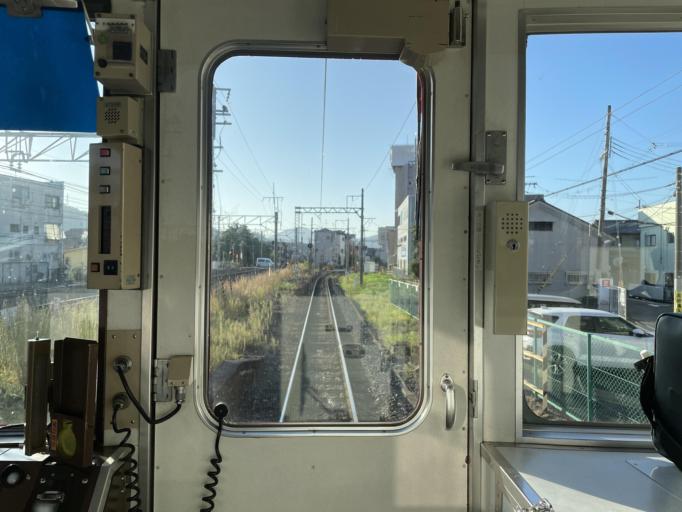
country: JP
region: Osaka
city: Kashihara
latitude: 34.5854
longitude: 135.6243
